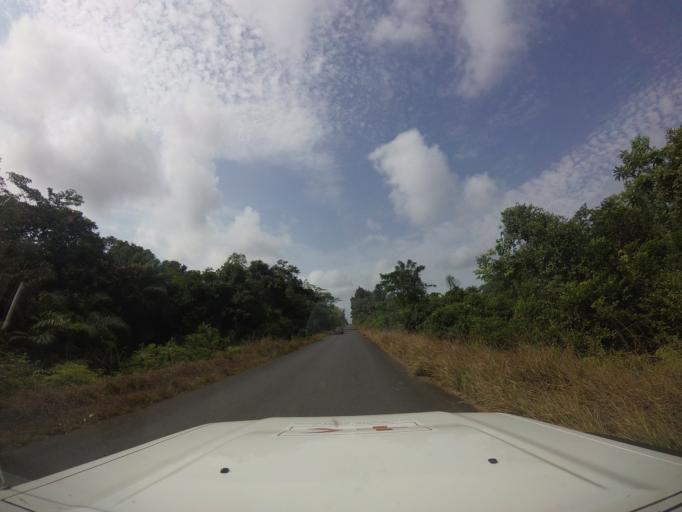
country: LR
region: Bomi
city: Tubmanburg
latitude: 6.7159
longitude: -10.8681
